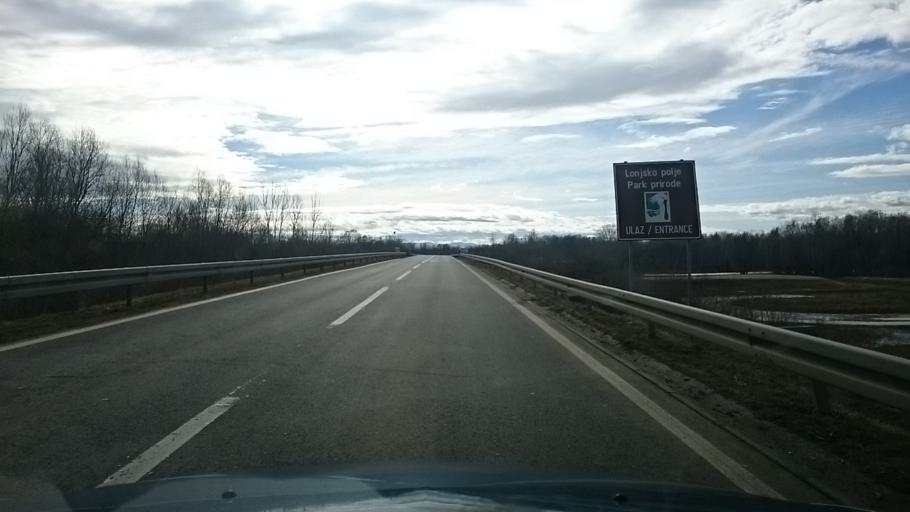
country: HR
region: Sisacko-Moslavacka
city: Novska
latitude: 45.2980
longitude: 16.9507
